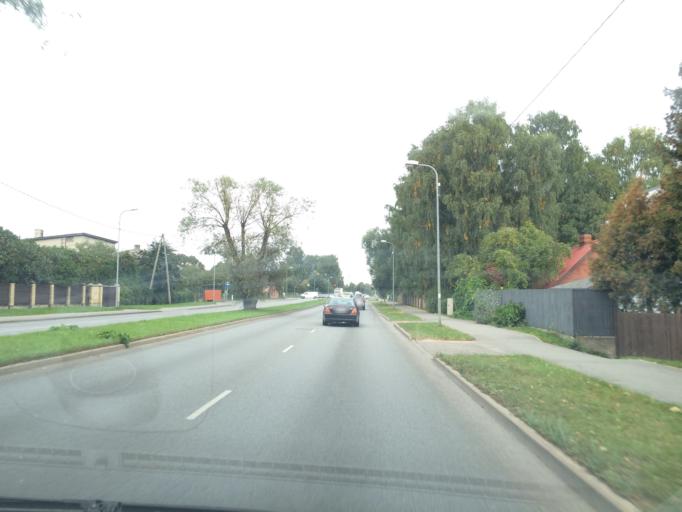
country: LV
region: Riga
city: Riga
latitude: 56.9440
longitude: 24.1828
